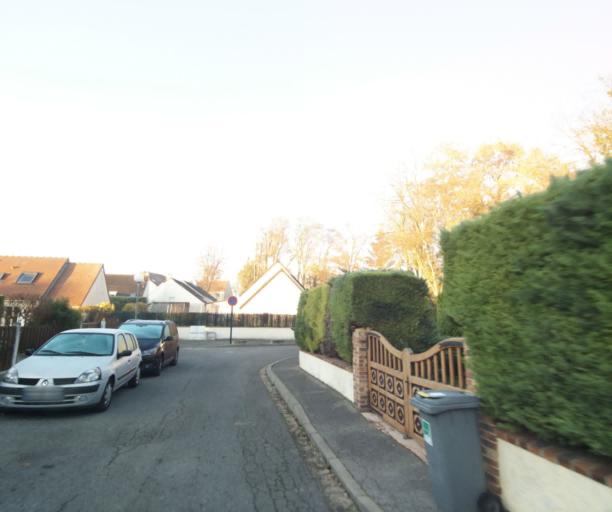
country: FR
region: Ile-de-France
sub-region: Departement du Val-d'Oise
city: Gonesse
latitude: 48.9835
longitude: 2.4467
